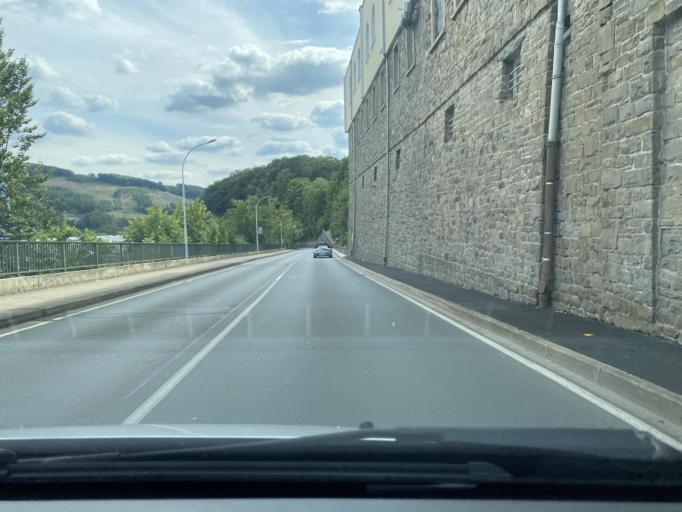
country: DE
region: North Rhine-Westphalia
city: Werdohl
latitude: 51.2597
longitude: 7.7696
